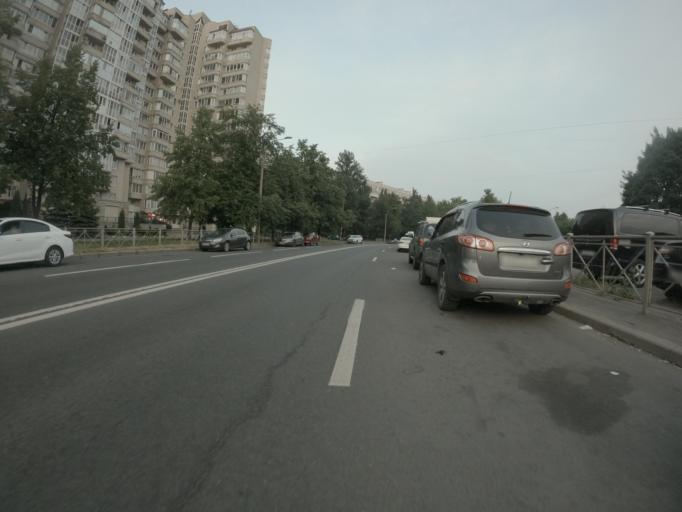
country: RU
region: St.-Petersburg
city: Krasnogvargeisky
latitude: 59.9664
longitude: 30.4305
